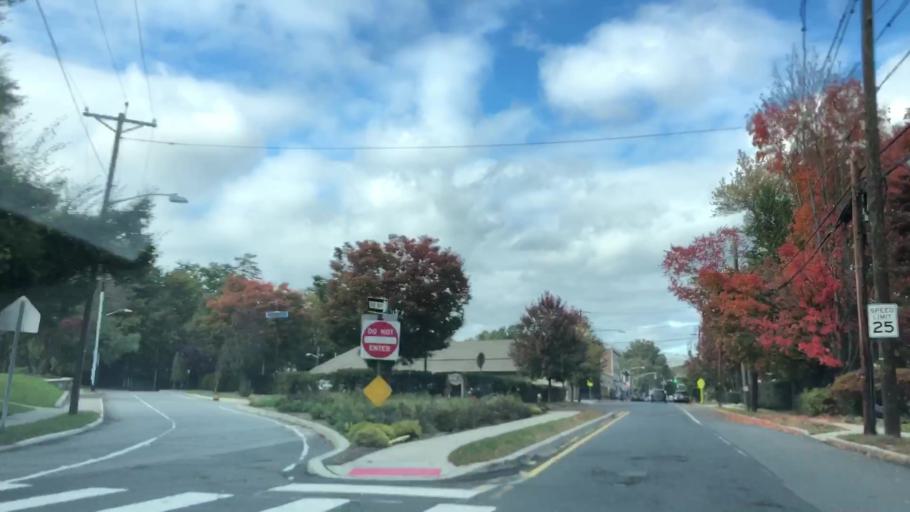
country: US
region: New Jersey
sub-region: Essex County
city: Glen Ridge
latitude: 40.7956
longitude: -74.2186
